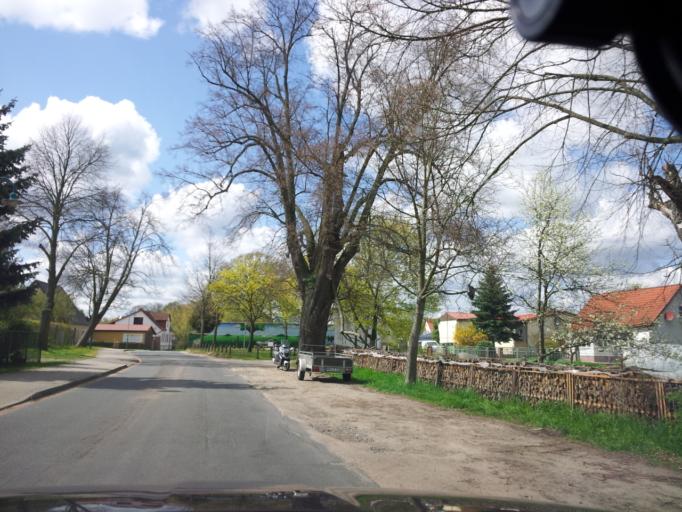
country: DE
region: Brandenburg
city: Rudnitz
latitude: 52.7223
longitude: 13.6212
